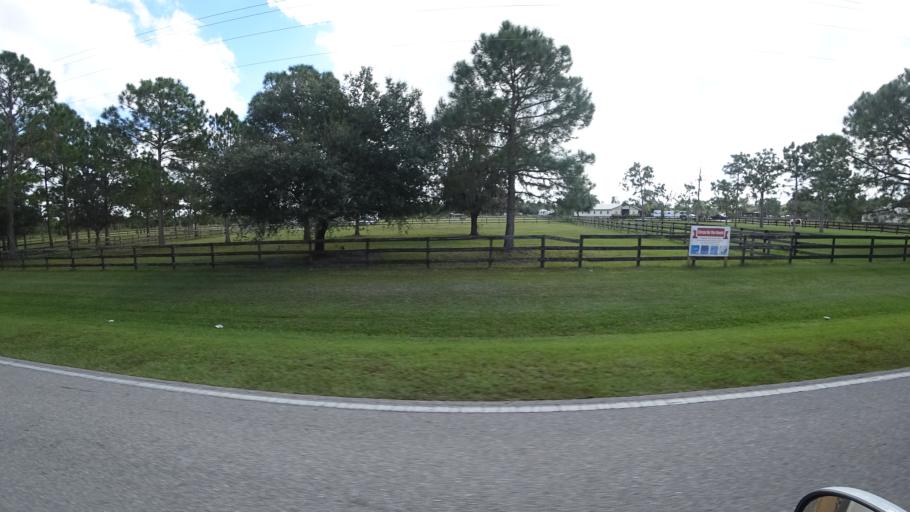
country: US
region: Florida
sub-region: Sarasota County
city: Lake Sarasota
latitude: 27.3620
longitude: -82.1535
